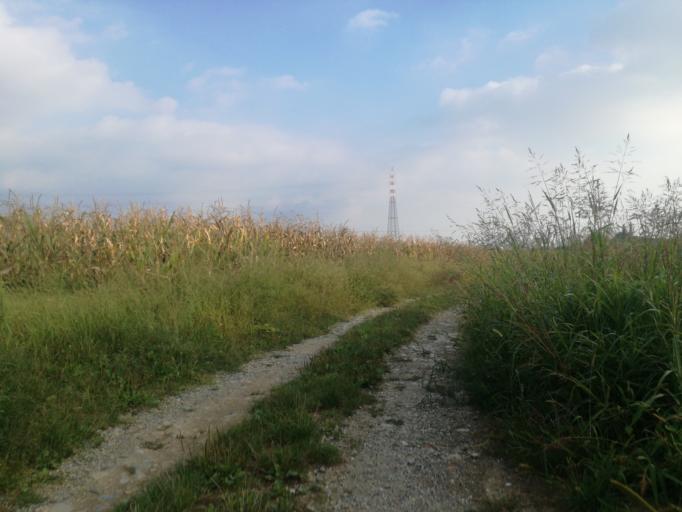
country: IT
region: Lombardy
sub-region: Provincia di Monza e Brianza
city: Porto d'Adda
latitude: 45.6606
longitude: 9.4598
